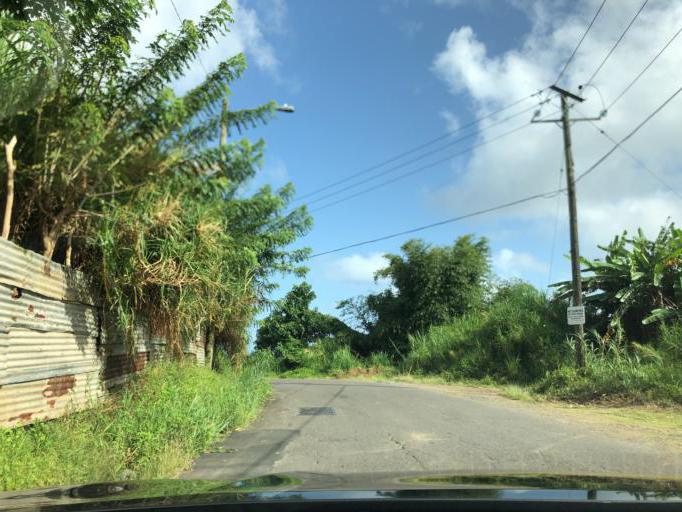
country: LC
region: Castries Quarter
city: Bisee
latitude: 13.9935
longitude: -60.9678
